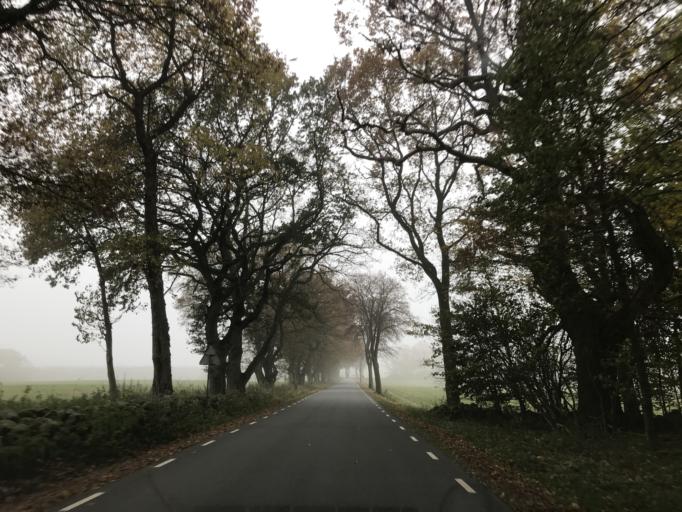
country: SE
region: Skane
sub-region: Svalovs Kommun
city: Kagerod
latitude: 55.9682
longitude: 13.0508
